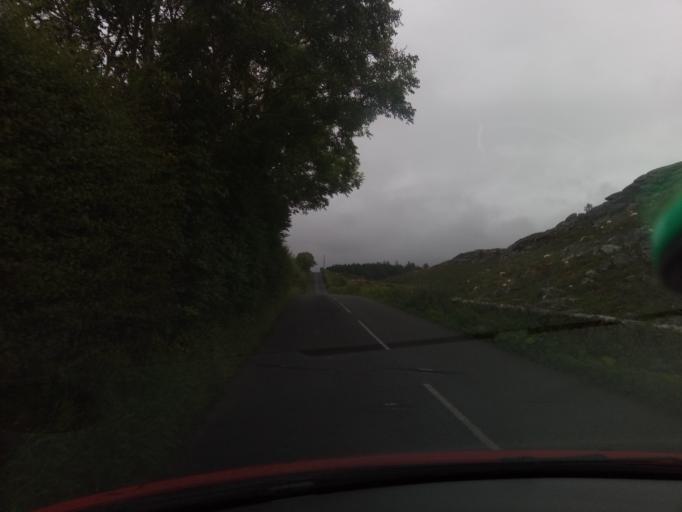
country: GB
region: England
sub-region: Northumberland
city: Rothley
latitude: 55.1920
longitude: -1.9372
